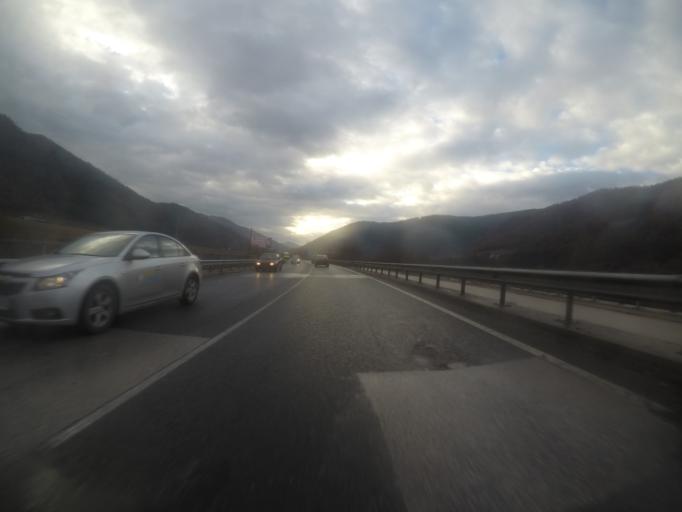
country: BG
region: Blagoevgrad
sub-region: Obshtina Simitli
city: Simitli
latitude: 41.9313
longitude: 23.1037
